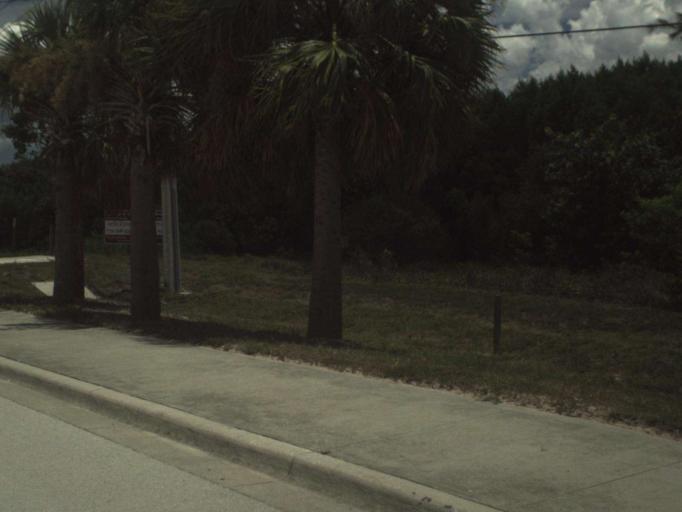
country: US
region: Florida
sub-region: Martin County
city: Jensen Beach
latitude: 27.2556
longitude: -80.2102
